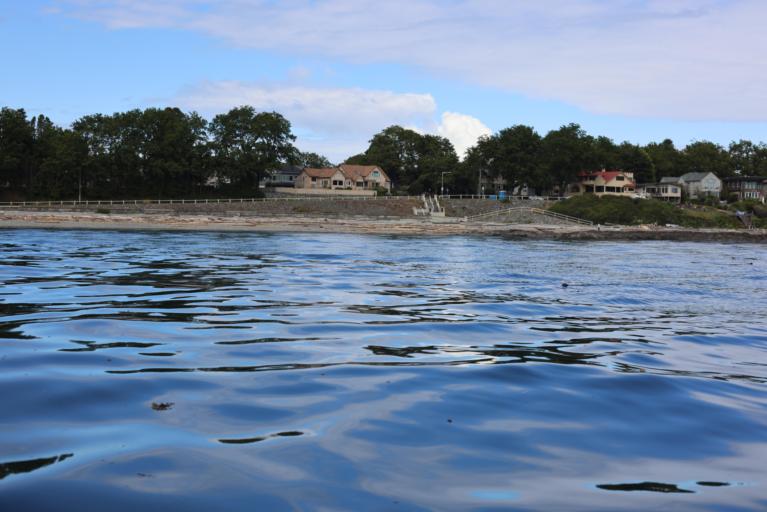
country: CA
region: British Columbia
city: Victoria
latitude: 48.4083
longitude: -123.3394
